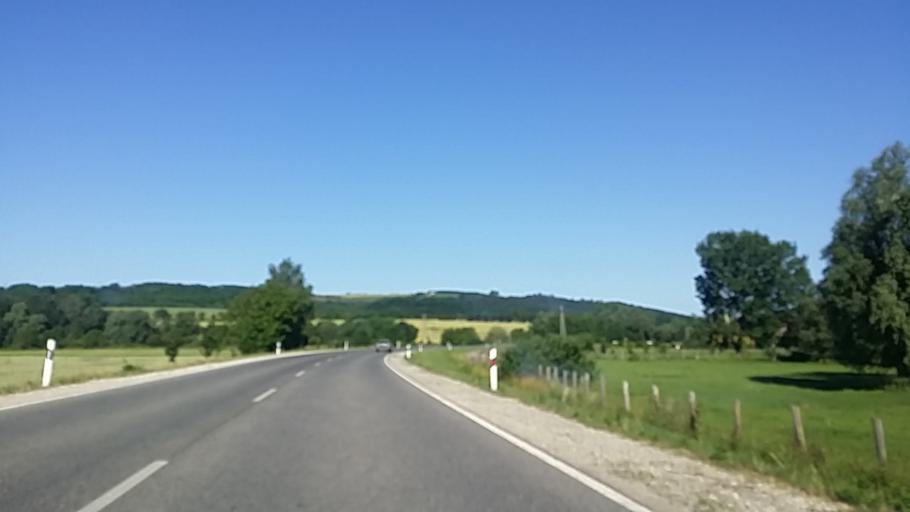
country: HU
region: Zala
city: Heviz
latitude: 46.8012
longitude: 17.1099
